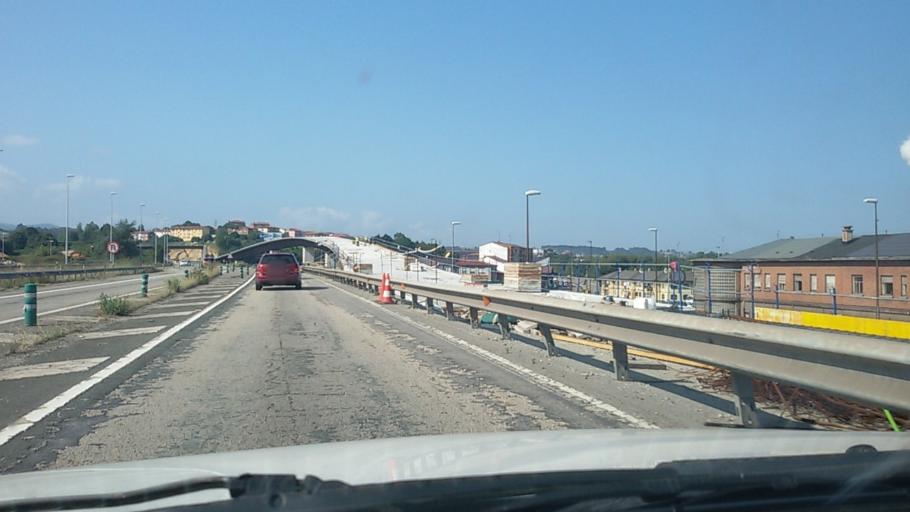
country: ES
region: Asturias
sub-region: Province of Asturias
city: Aviles
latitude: 43.5525
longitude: -5.8970
